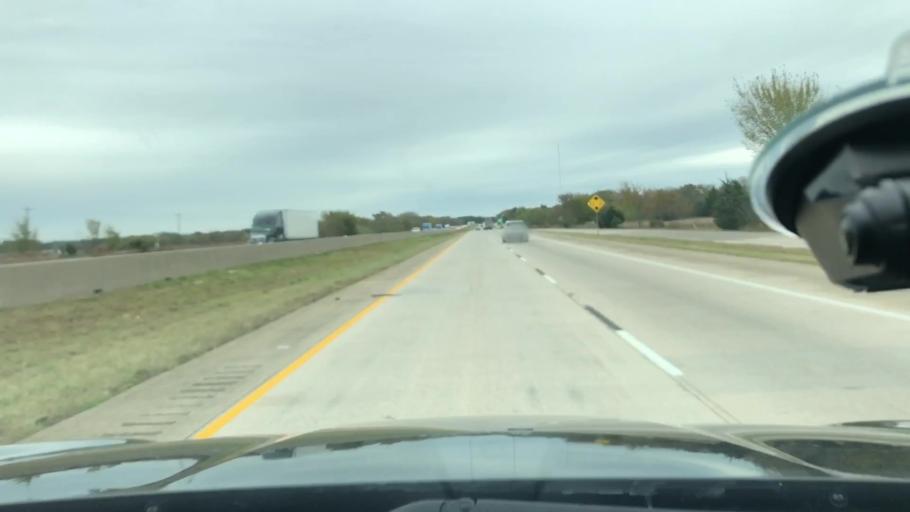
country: US
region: Texas
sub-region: Hopkins County
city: Sulphur Springs
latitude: 33.1281
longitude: -95.7570
